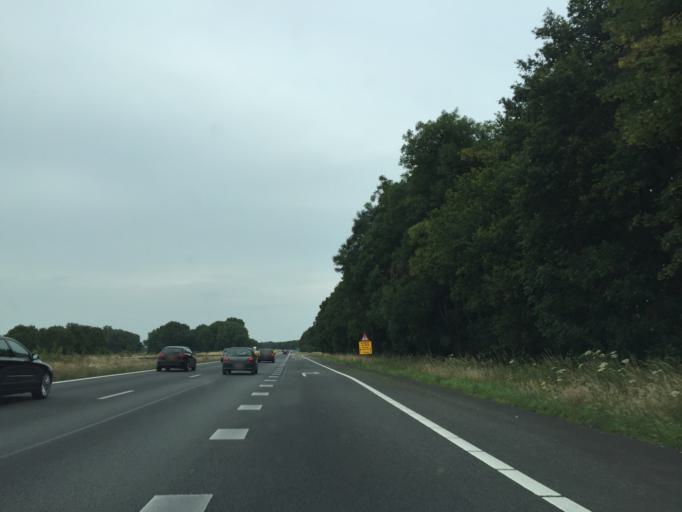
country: NL
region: North Brabant
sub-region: Gemeente Landerd
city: Schaijk
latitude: 51.7852
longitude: 5.6473
